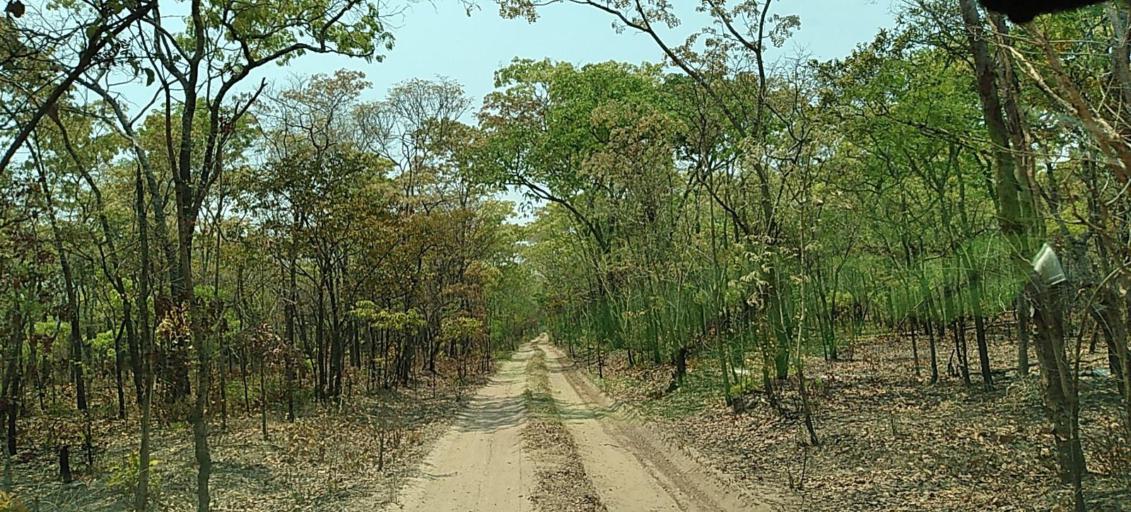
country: ZM
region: North-Western
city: Kabompo
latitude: -13.6470
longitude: 24.4801
